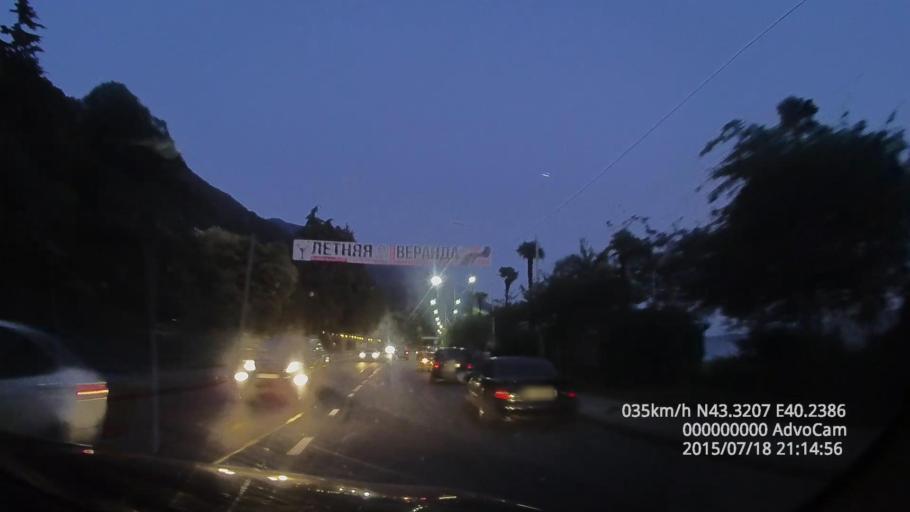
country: GE
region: Abkhazia
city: Gagra
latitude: 43.3206
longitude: 40.2388
